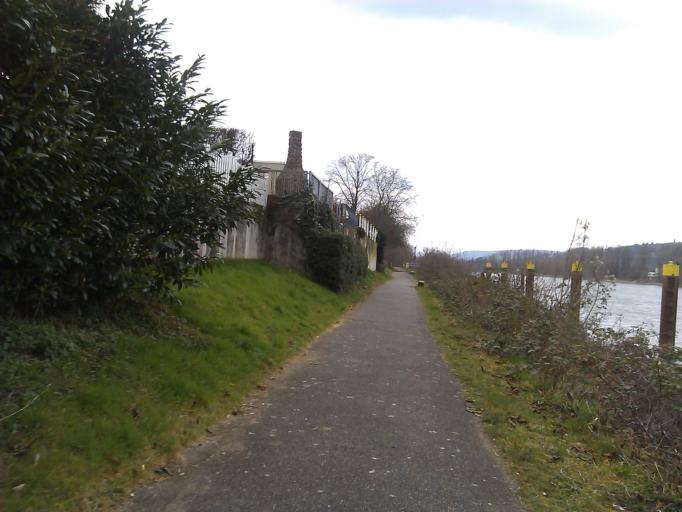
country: DE
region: Rheinland-Pfalz
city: Niederwerth
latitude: 50.3870
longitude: 7.6066
